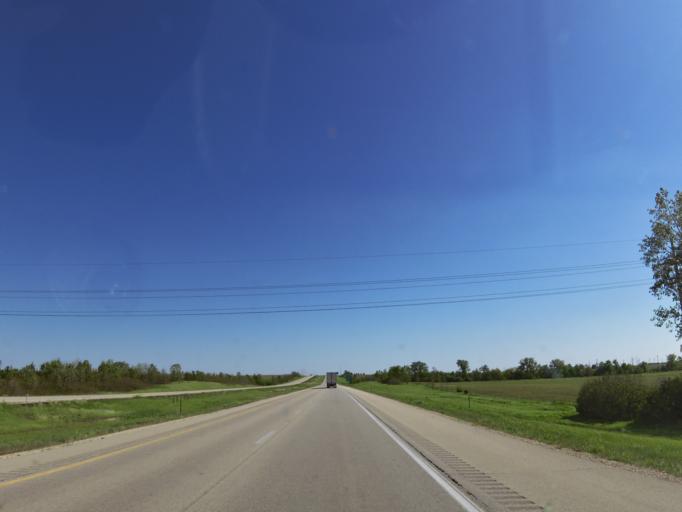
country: US
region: Illinois
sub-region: Ogle County
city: Rochelle
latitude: 41.7759
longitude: -89.0103
